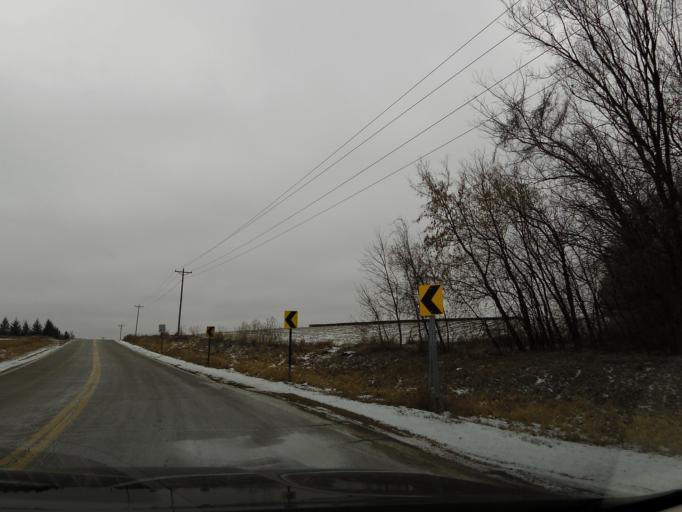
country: US
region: Minnesota
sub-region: Hennepin County
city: Medina
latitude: 45.0402
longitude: -93.5776
